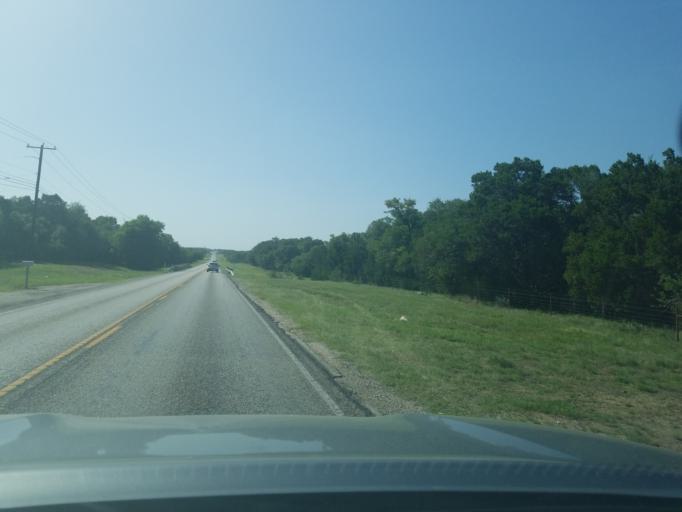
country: US
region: Texas
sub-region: Comal County
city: Garden Ridge
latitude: 29.6773
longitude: -98.3207
